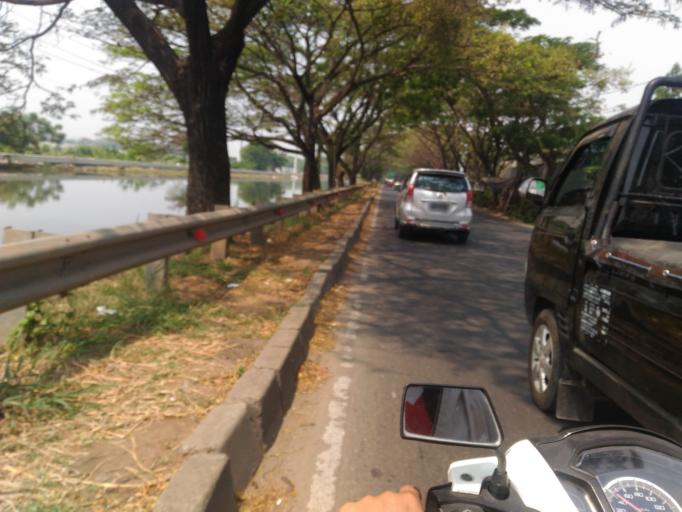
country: ID
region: Banten
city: Tangerang
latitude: -6.1561
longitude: 106.6077
